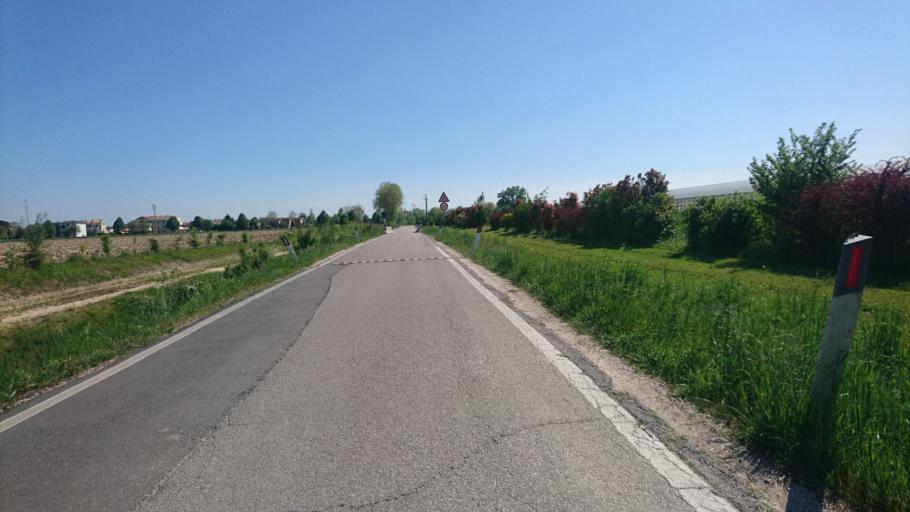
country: IT
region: Veneto
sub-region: Provincia di Venezia
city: Marcon-Gaggio-Colmello
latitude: 45.5676
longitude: 12.2910
